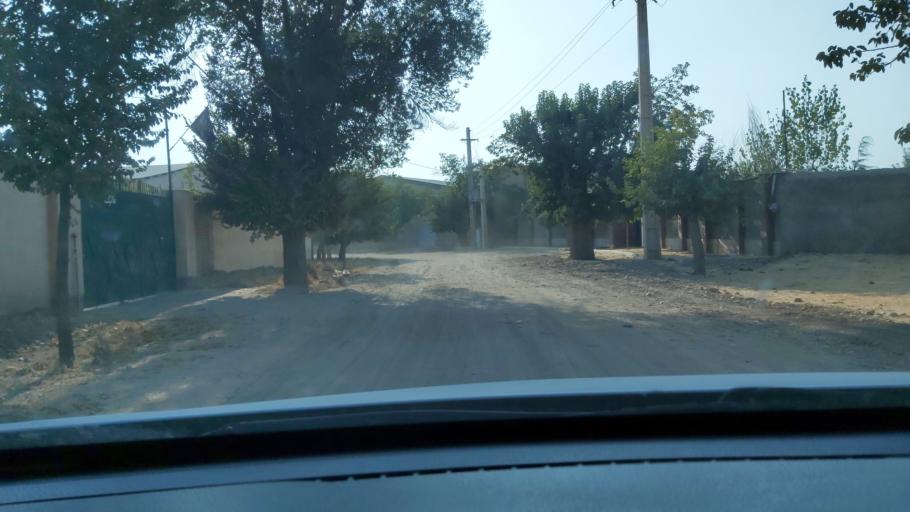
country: IR
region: Alborz
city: Hashtgerd
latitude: 35.9548
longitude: 50.7834
